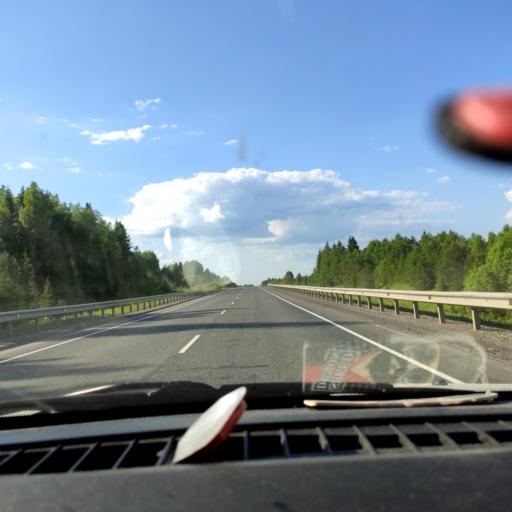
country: RU
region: Perm
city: Kudymkar
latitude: 58.6865
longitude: 54.6981
